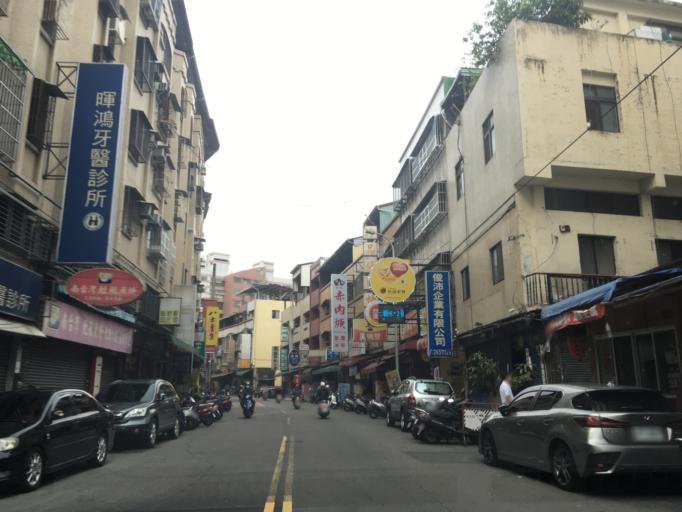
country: TW
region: Taiwan
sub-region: Taichung City
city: Taichung
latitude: 24.1743
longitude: 120.6658
